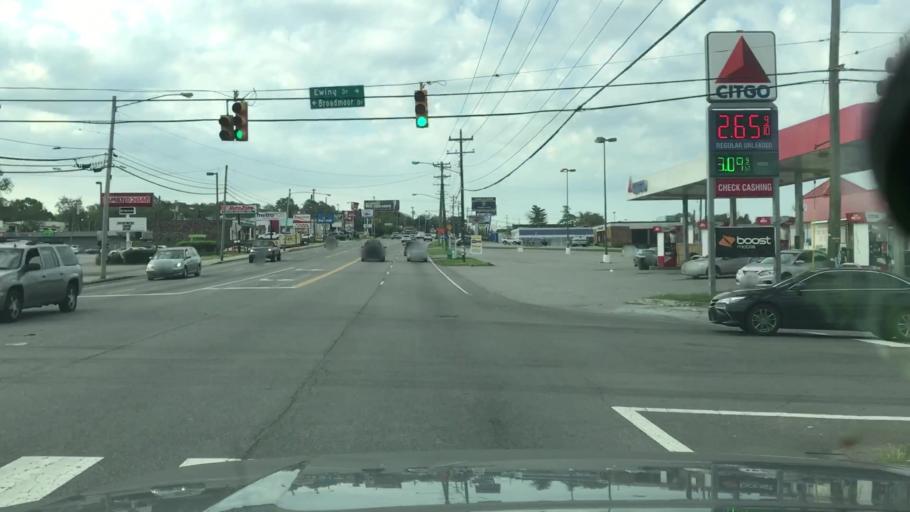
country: US
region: Tennessee
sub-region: Davidson County
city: Nashville
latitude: 36.2295
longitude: -86.7594
